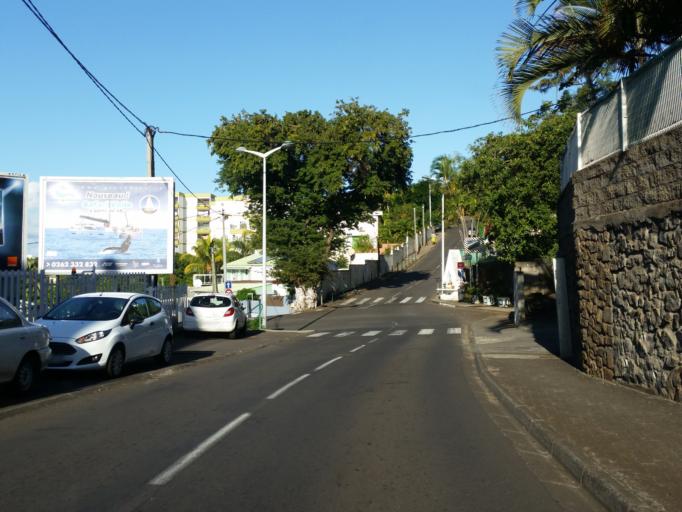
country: RE
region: Reunion
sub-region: Reunion
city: Saint-Denis
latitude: -20.8985
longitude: 55.4686
